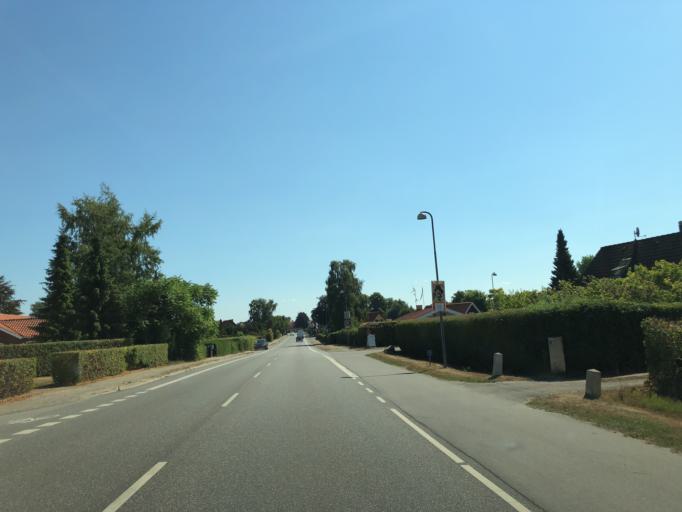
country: DK
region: Zealand
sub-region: Odsherred Kommune
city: Nykobing Sjaelland
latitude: 55.9430
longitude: 11.7455
